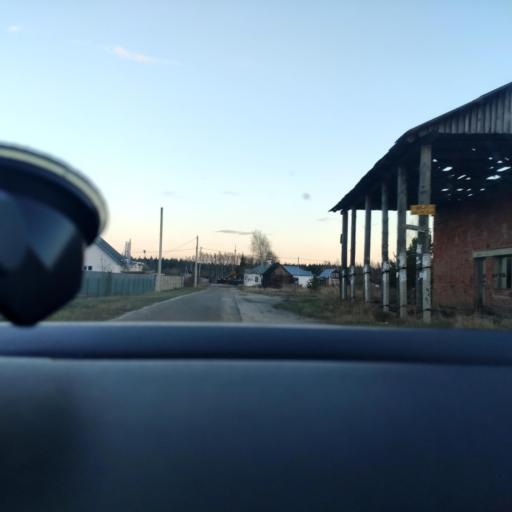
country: RU
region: Moskovskaya
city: Shaturtorf
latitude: 55.4354
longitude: 39.4270
